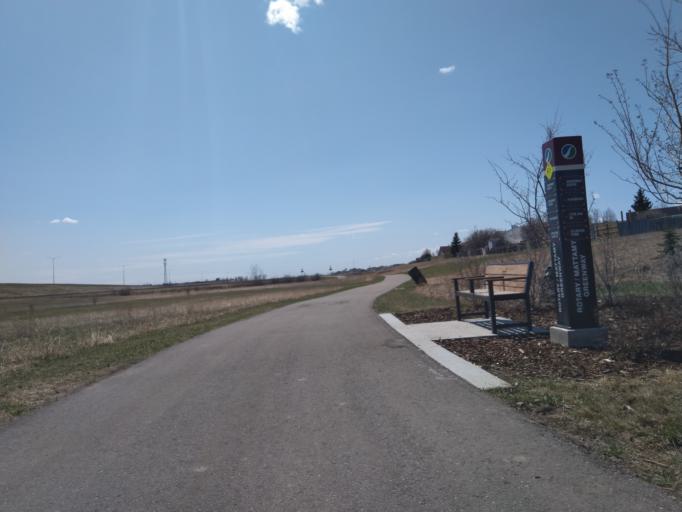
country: CA
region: Alberta
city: Chestermere
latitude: 51.0572
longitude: -113.9231
